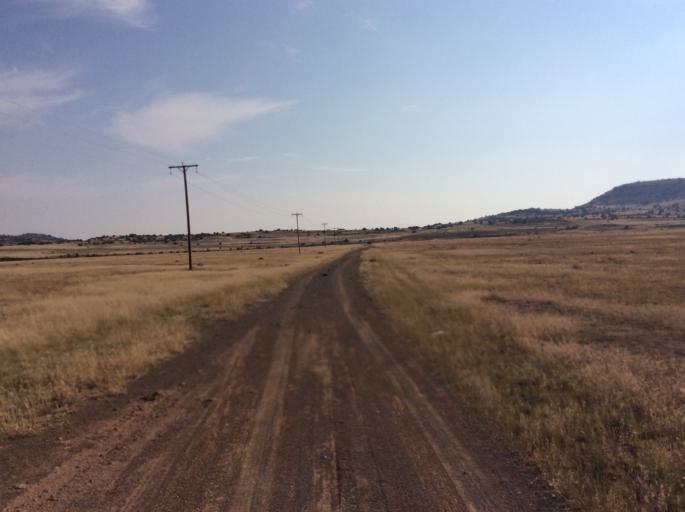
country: LS
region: Mafeteng
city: Mafeteng
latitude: -29.7086
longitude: 27.0087
